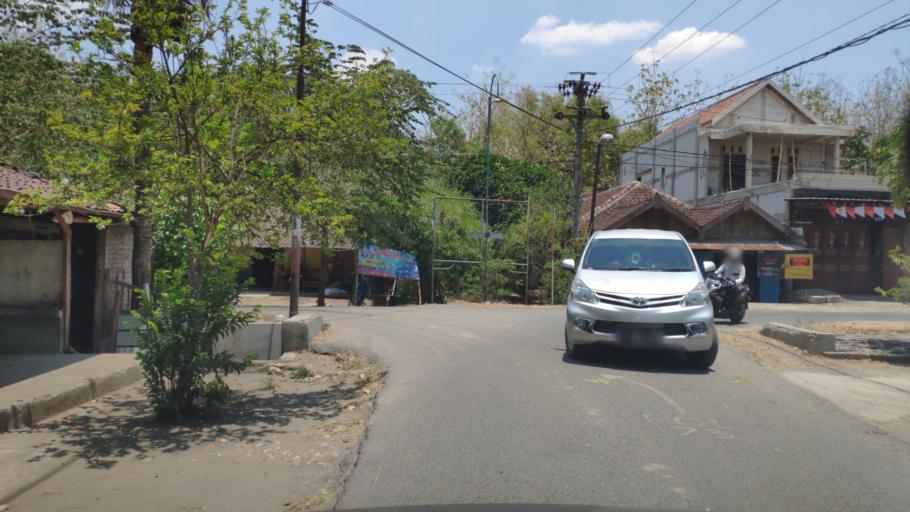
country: ID
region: Central Java
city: Kapuan
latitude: -7.1996
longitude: 111.5539
